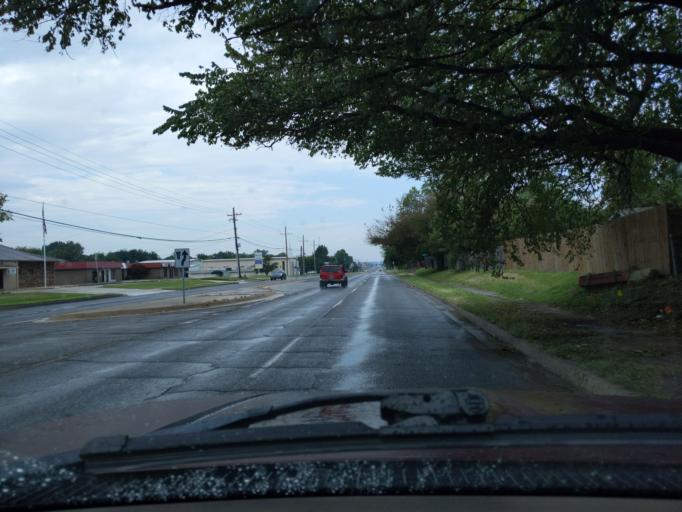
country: US
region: Oklahoma
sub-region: Tulsa County
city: Broken Arrow
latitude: 36.1335
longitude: -95.8361
